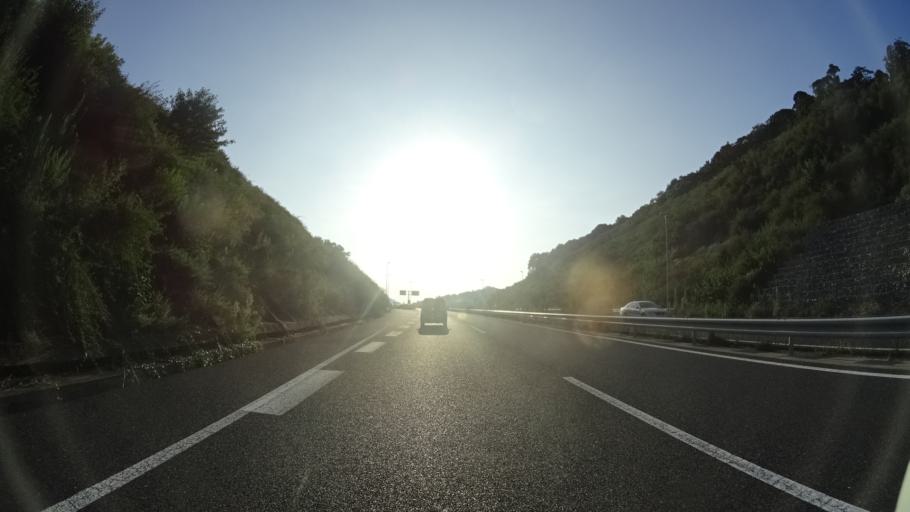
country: JP
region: Yamaguchi
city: Hagi
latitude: 34.3890
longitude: 131.3279
